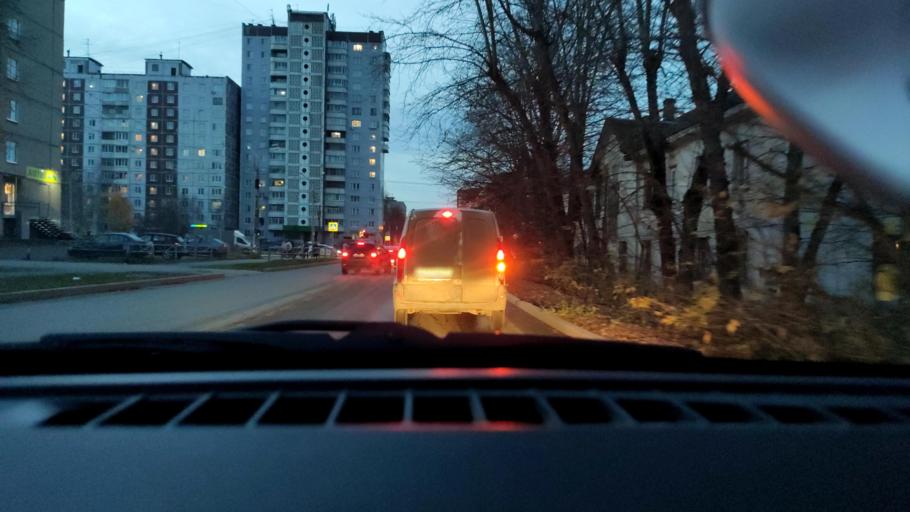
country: RU
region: Perm
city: Kondratovo
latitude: 57.9987
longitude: 56.1469
